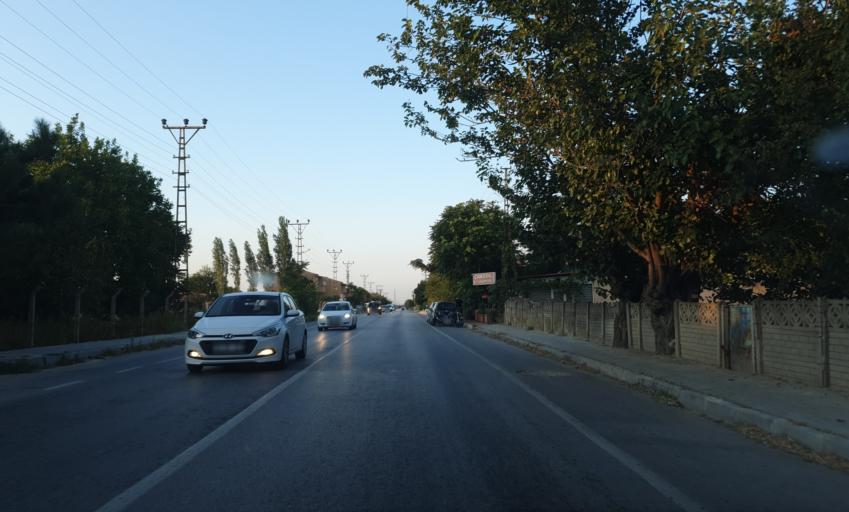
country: TR
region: Kirklareli
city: Luleburgaz
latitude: 41.4620
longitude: 27.3900
